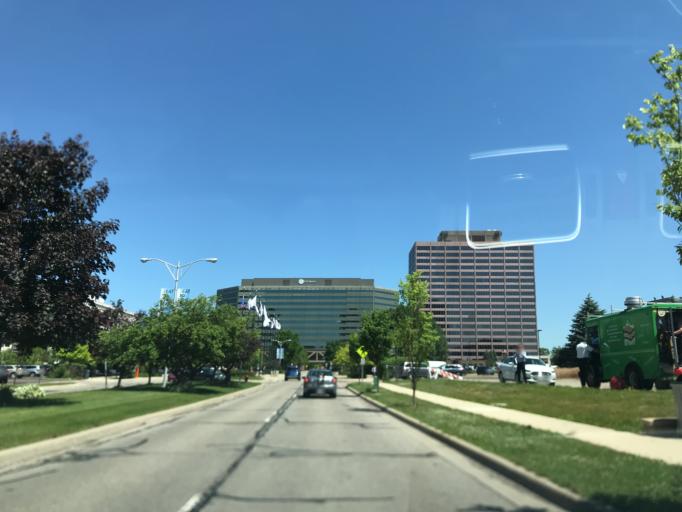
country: US
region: Michigan
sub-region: Oakland County
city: Southfield
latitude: 42.4807
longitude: -83.2439
